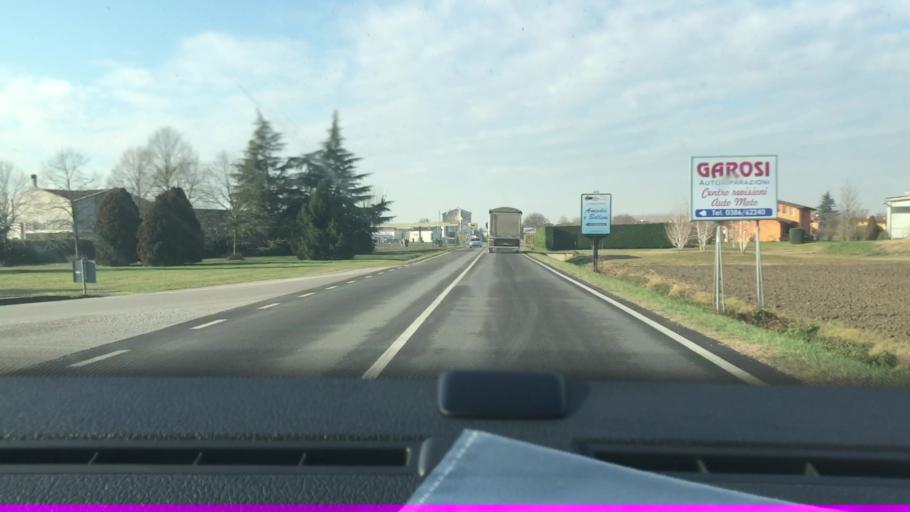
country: IT
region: Lombardy
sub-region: Provincia di Mantova
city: Sermide
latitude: 45.0095
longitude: 11.2794
